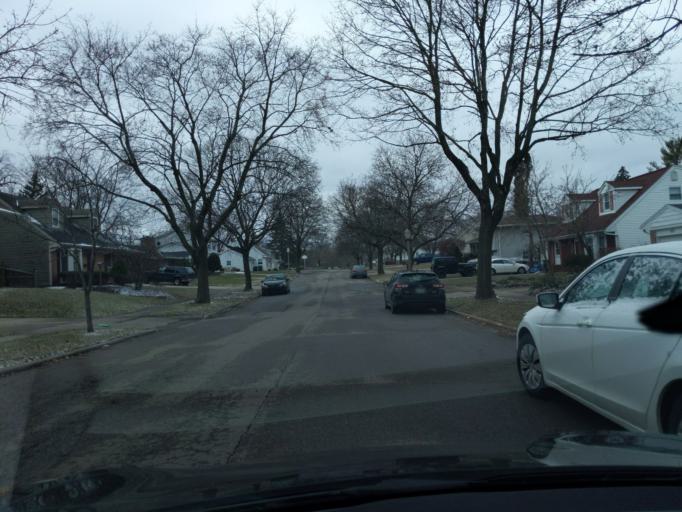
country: US
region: Michigan
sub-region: Ingham County
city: East Lansing
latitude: 42.7557
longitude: -84.5148
